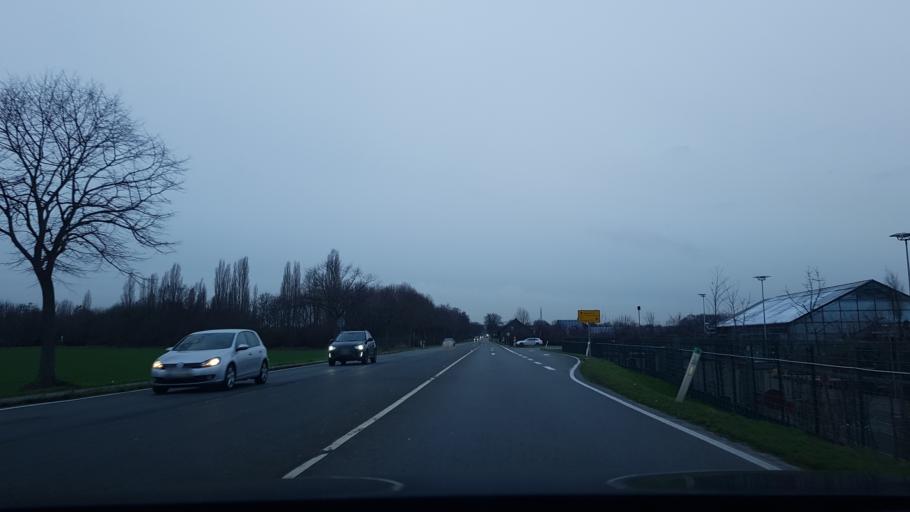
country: DE
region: North Rhine-Westphalia
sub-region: Regierungsbezirk Dusseldorf
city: Moers
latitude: 51.4118
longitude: 6.6612
